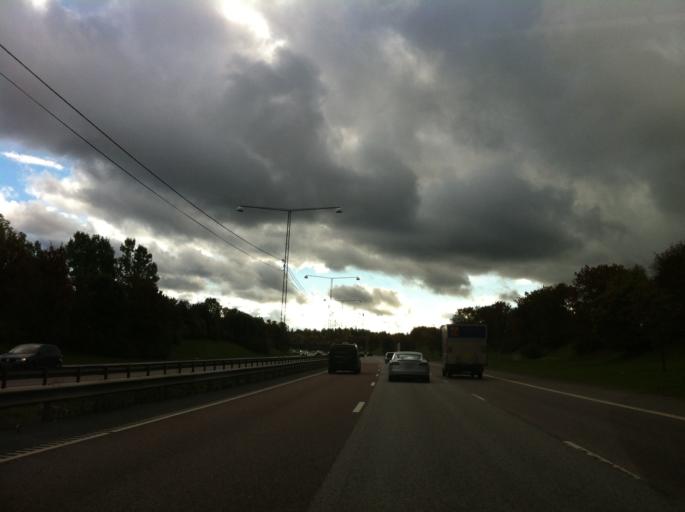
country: SE
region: Stockholm
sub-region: Upplands Vasby Kommun
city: Upplands Vaesby
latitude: 59.4693
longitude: 17.9123
